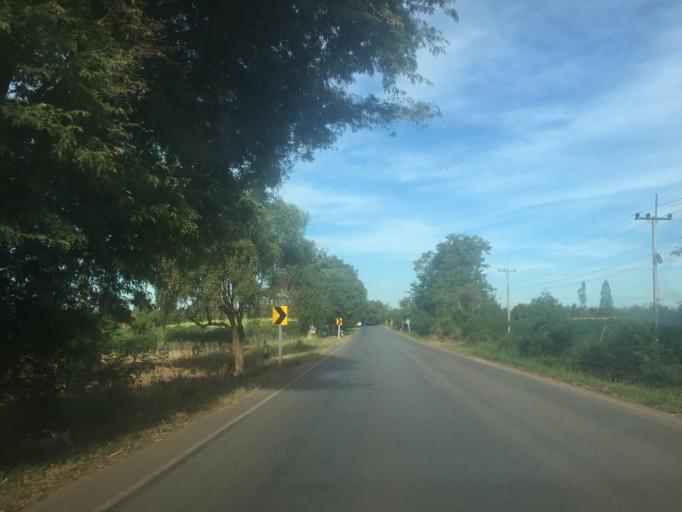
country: TH
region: Changwat Udon Thani
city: Si That
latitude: 16.9863
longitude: 103.1778
